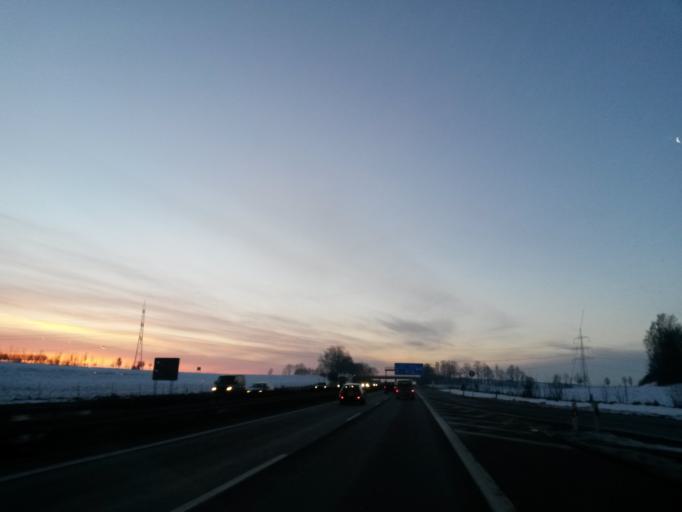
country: DE
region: Bavaria
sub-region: Swabia
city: Buxheim
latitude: 48.0122
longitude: 10.1396
